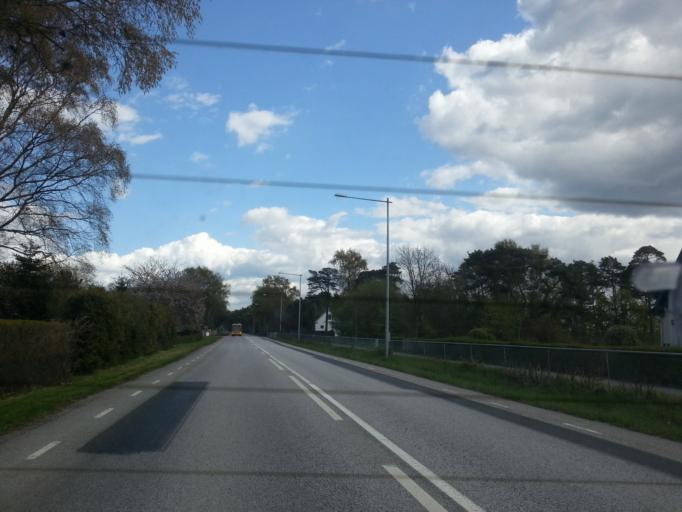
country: SE
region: Skane
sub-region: Ystads Kommun
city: Kopingebro
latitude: 55.4329
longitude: 13.9433
